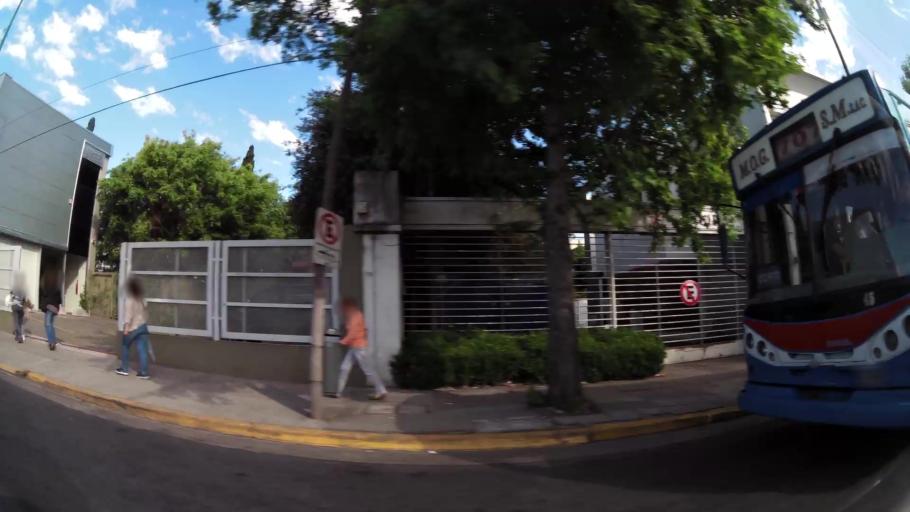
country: AR
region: Buenos Aires
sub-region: Partido de San Isidro
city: San Isidro
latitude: -34.4950
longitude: -58.5518
